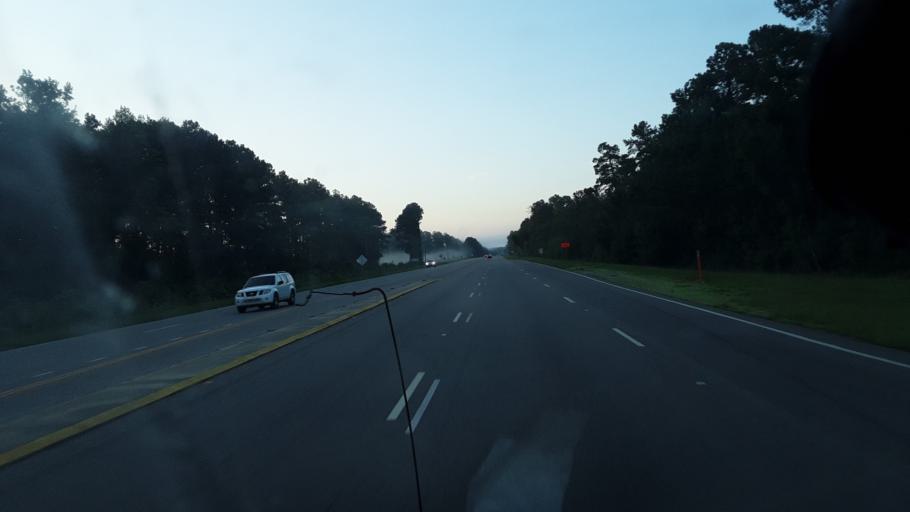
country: US
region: South Carolina
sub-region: Clarendon County
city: Manning
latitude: 33.7375
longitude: -80.2071
